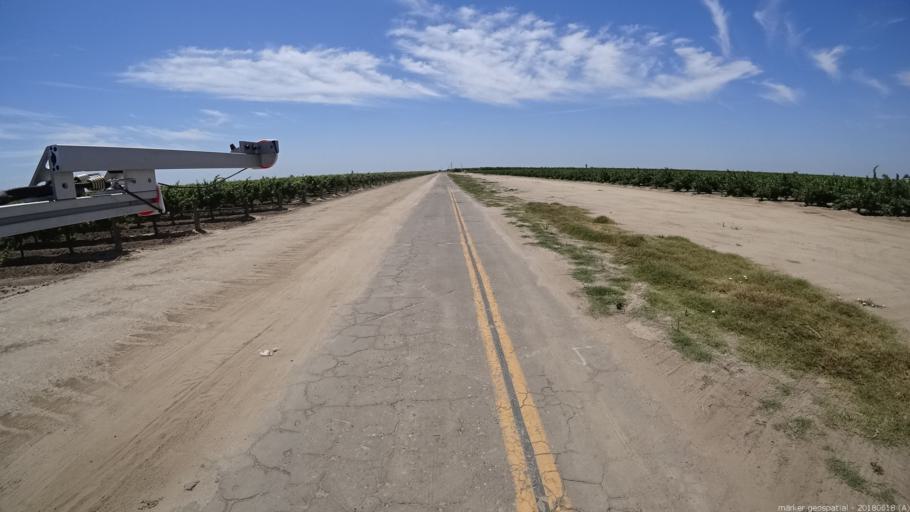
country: US
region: California
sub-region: Madera County
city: Parkwood
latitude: 36.8728
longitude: -120.1013
